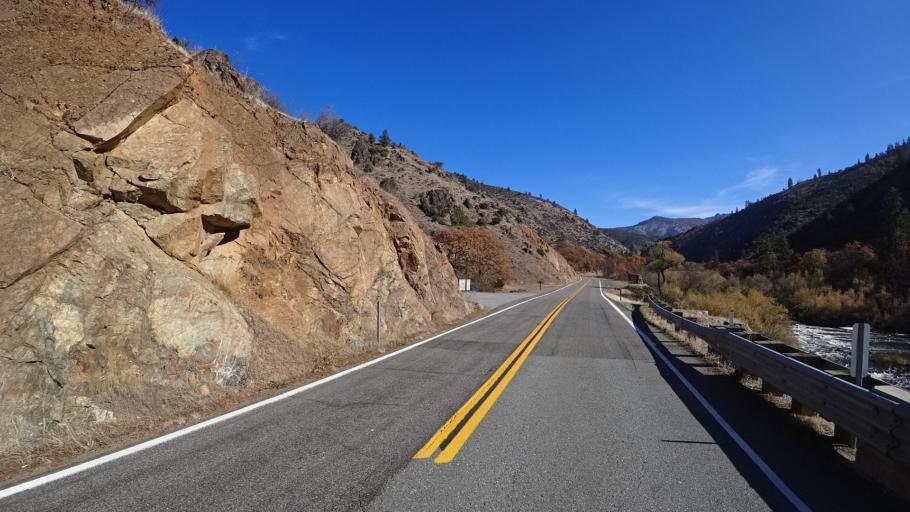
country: US
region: California
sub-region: Siskiyou County
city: Yreka
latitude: 41.8339
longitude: -122.6205
